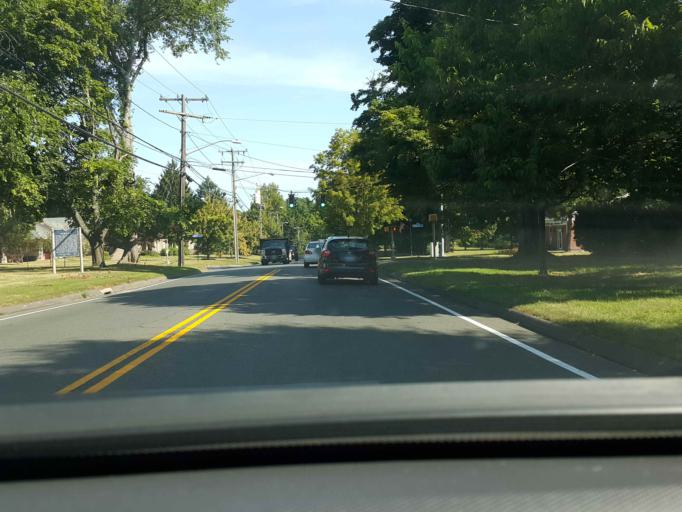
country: US
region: Connecticut
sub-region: Middlesex County
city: Durham
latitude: 41.4708
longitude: -72.6803
